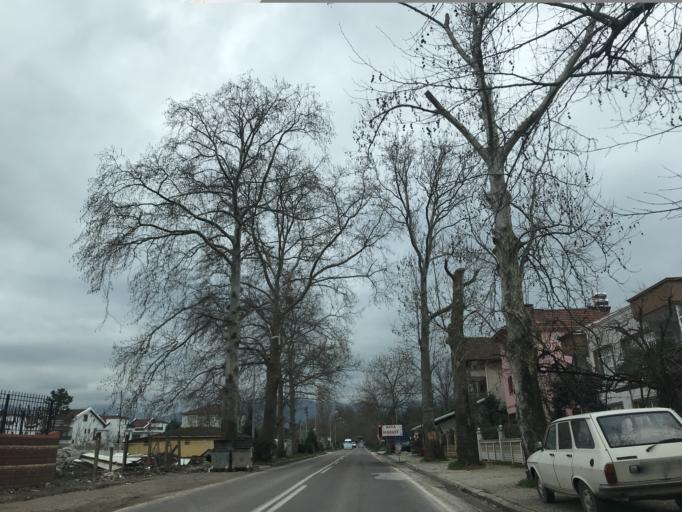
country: TR
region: Yalova
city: Kadikoy
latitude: 40.6405
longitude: 29.2280
